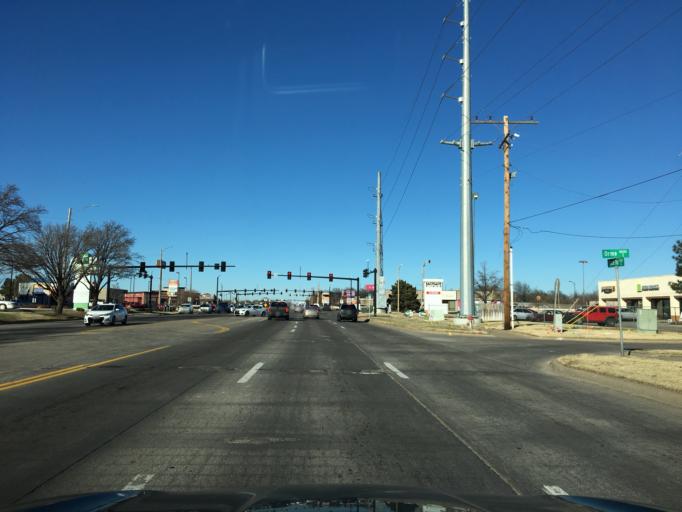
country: US
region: Kansas
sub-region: Sedgwick County
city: Bellaire
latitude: 37.6770
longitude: -97.2444
